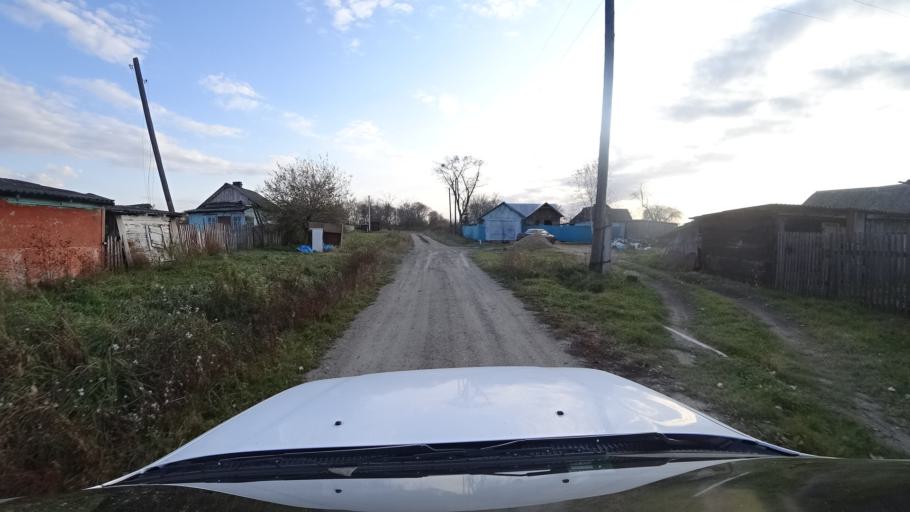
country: RU
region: Primorskiy
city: Lazo
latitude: 45.8243
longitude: 133.6102
